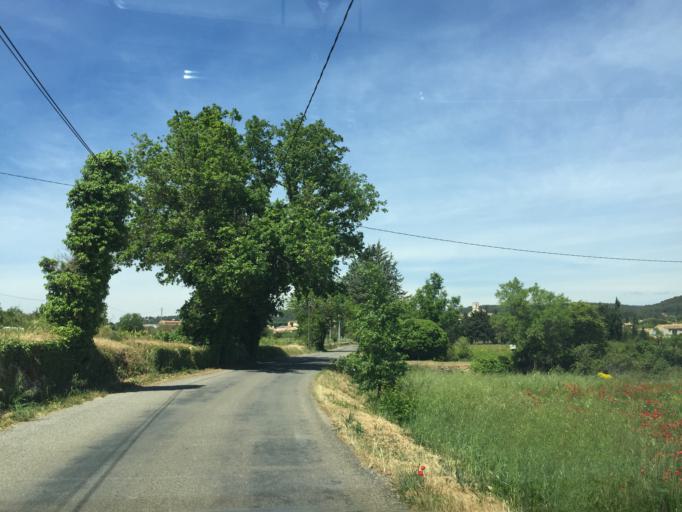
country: FR
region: Provence-Alpes-Cote d'Azur
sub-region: Departement du Var
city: Lorgues
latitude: 43.4838
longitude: 6.3640
